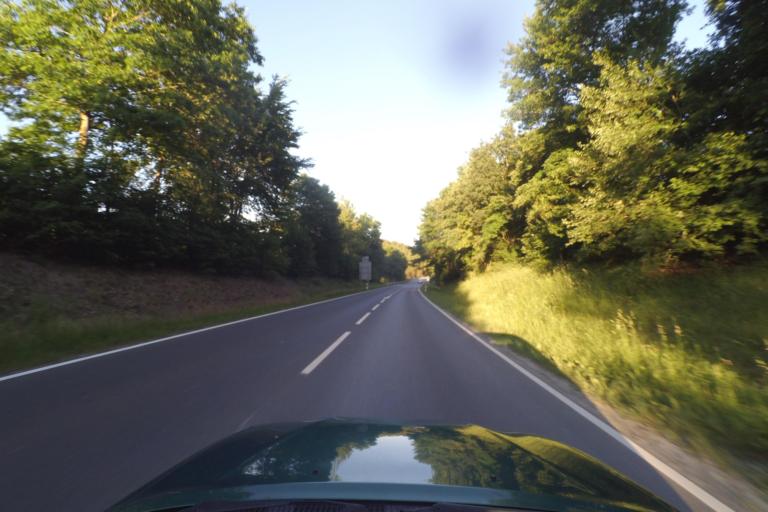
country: DE
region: Bavaria
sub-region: Upper Palatinate
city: Windischeschenbach
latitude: 49.8077
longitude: 12.1590
